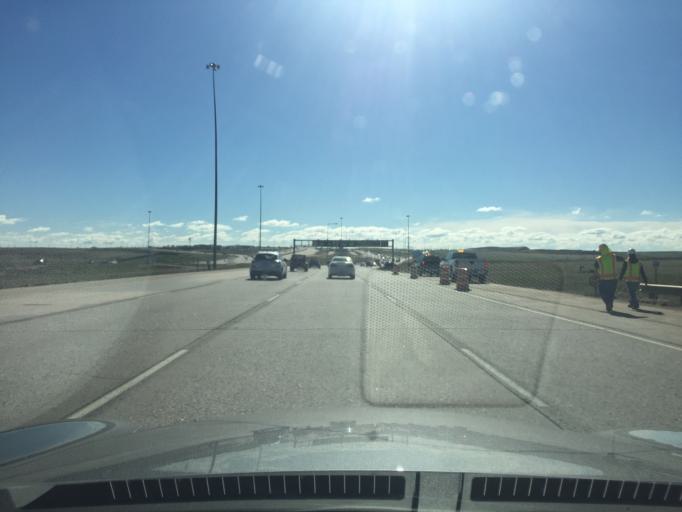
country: US
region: Colorado
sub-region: Adams County
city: Aurora
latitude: 39.8338
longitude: -104.7344
